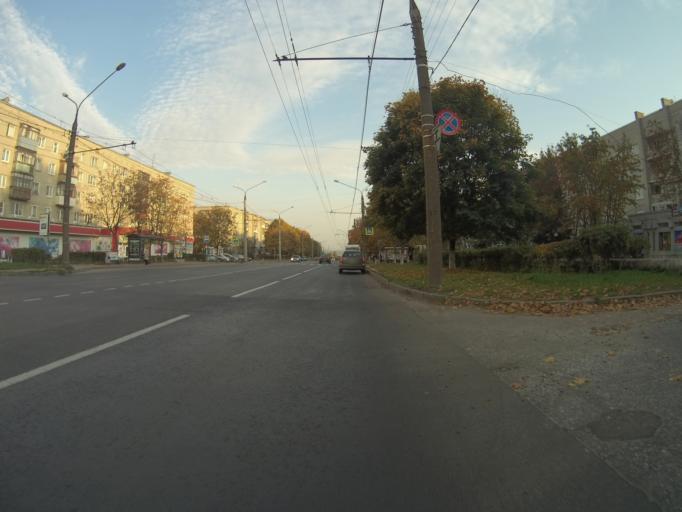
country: RU
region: Vladimir
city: Bogolyubovo
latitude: 56.1683
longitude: 40.4786
